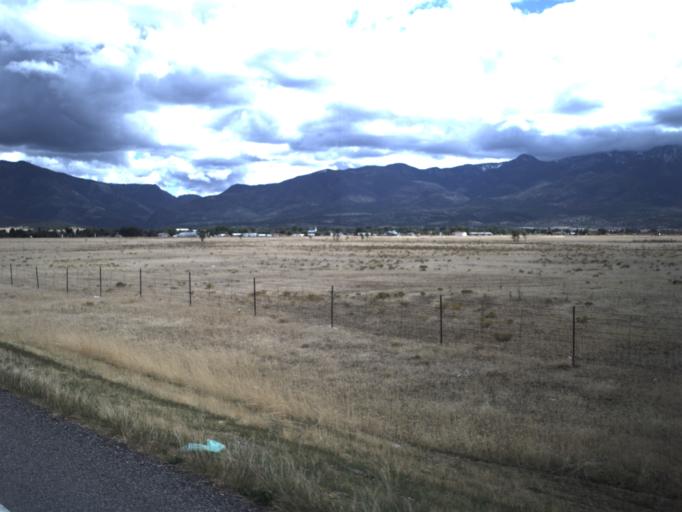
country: US
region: Utah
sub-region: Millard County
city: Fillmore
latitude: 38.9792
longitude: -112.3511
